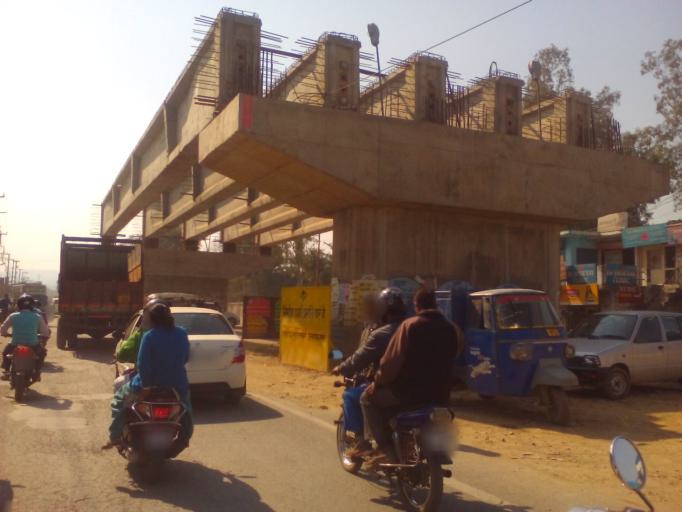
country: IN
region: Uttarakhand
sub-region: Dehradun
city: Clement Town
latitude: 30.2868
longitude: 77.9959
